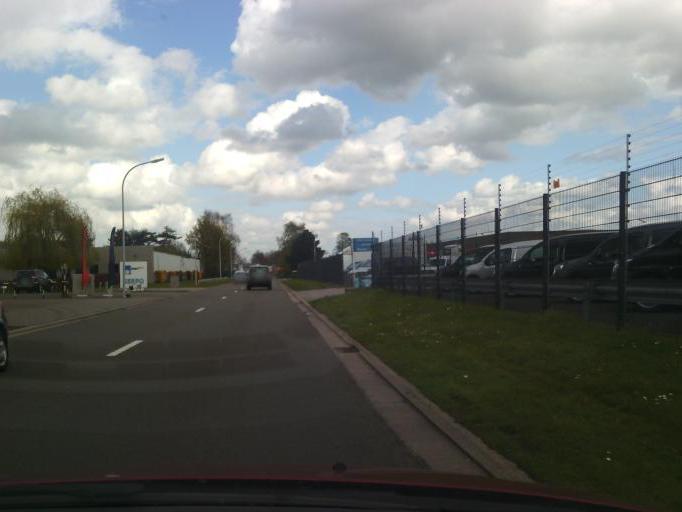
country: BE
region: Flanders
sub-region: Provincie Oost-Vlaanderen
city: Sint-Niklaas
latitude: 51.1465
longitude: 4.1658
